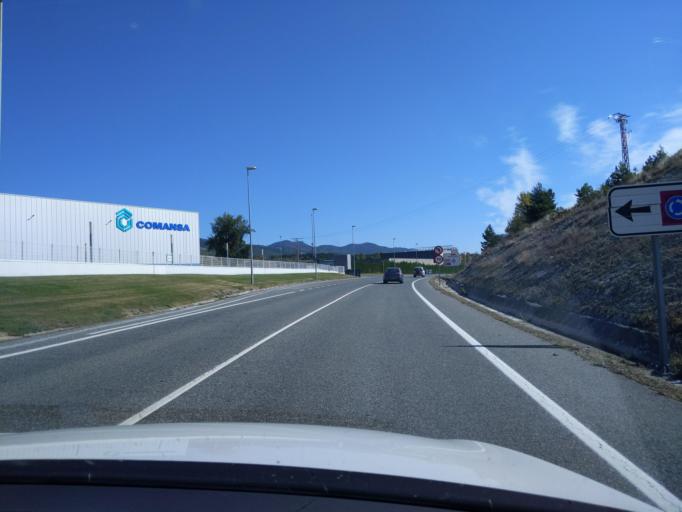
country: ES
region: Navarre
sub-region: Provincia de Navarra
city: Egues-Uharte
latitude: 42.8292
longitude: -1.5779
